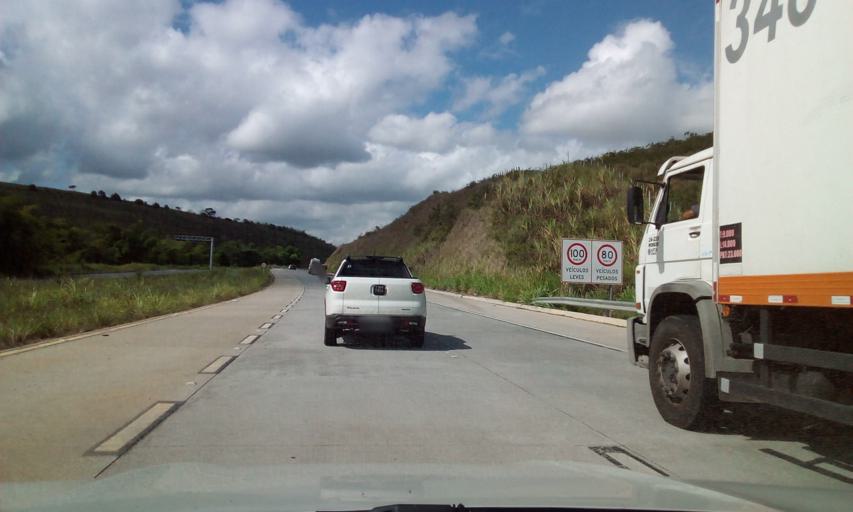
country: BR
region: Alagoas
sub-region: Messias
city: Messias
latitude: -9.3382
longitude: -35.8308
